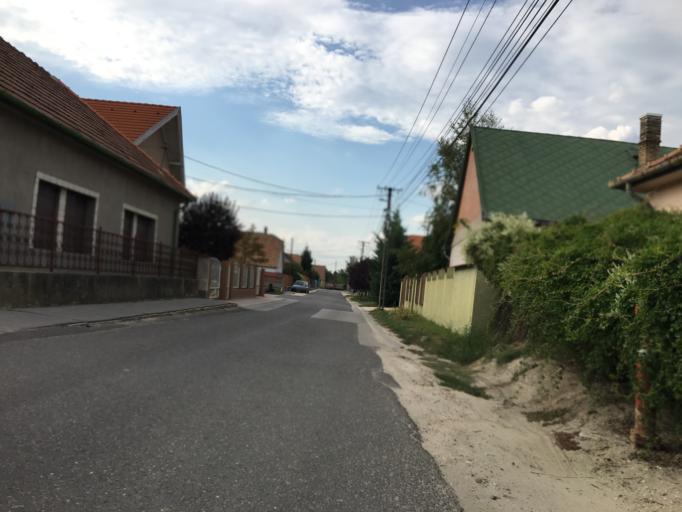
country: HU
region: Pest
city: Szigetszentmiklos
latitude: 47.3499
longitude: 19.0377
